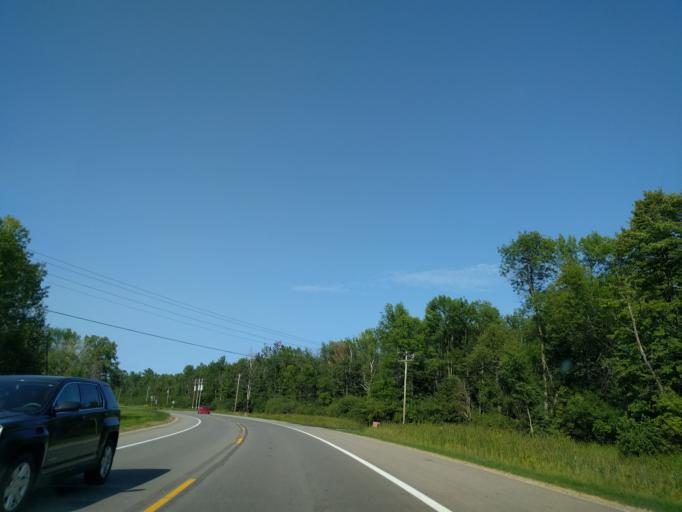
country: US
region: Michigan
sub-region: Menominee County
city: Menominee
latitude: 45.1569
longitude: -87.5921
